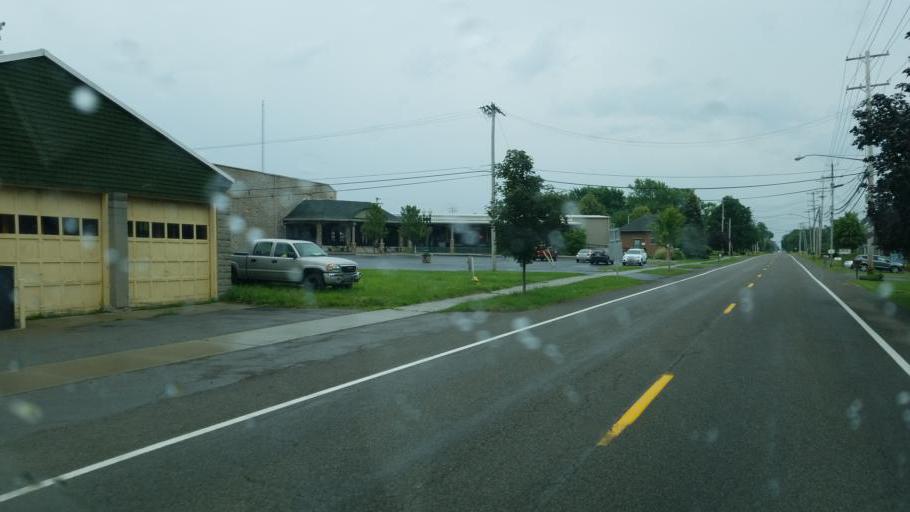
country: US
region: New York
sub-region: Niagara County
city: Wilson
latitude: 43.2993
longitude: -78.8260
